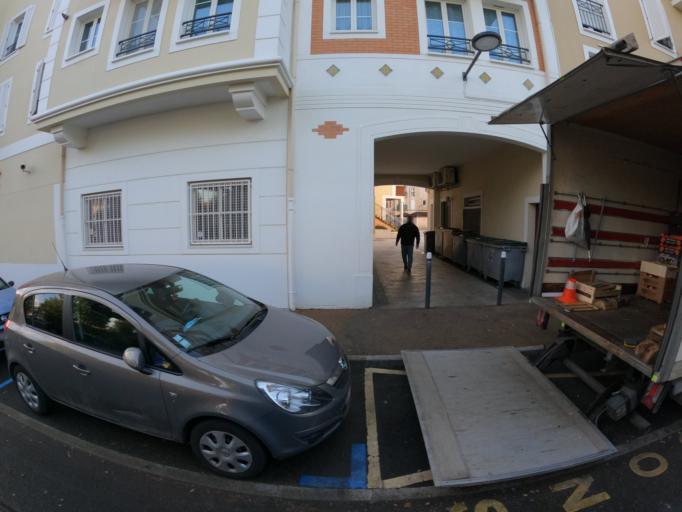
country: FR
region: Ile-de-France
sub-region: Departement de Seine-et-Marne
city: Bailly-Romainvilliers
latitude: 48.8508
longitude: 2.8202
